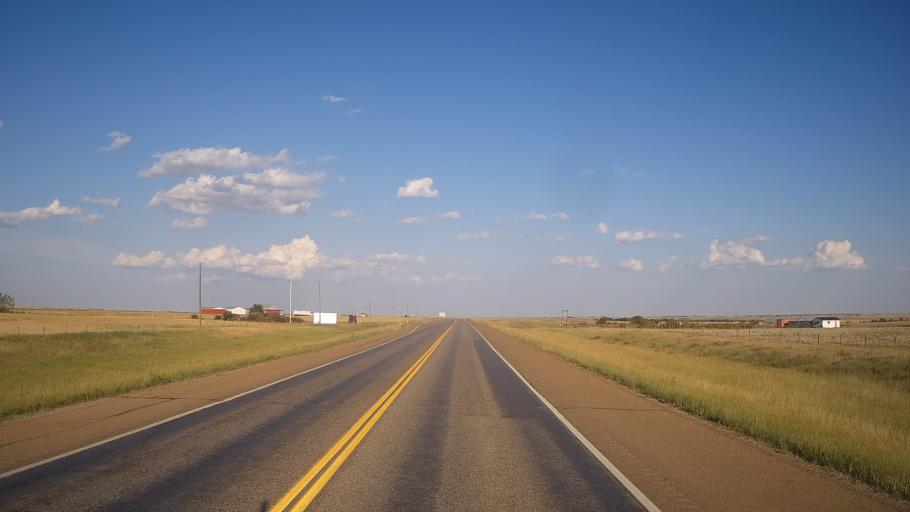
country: CA
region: Alberta
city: Hanna
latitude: 51.6290
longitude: -111.9093
